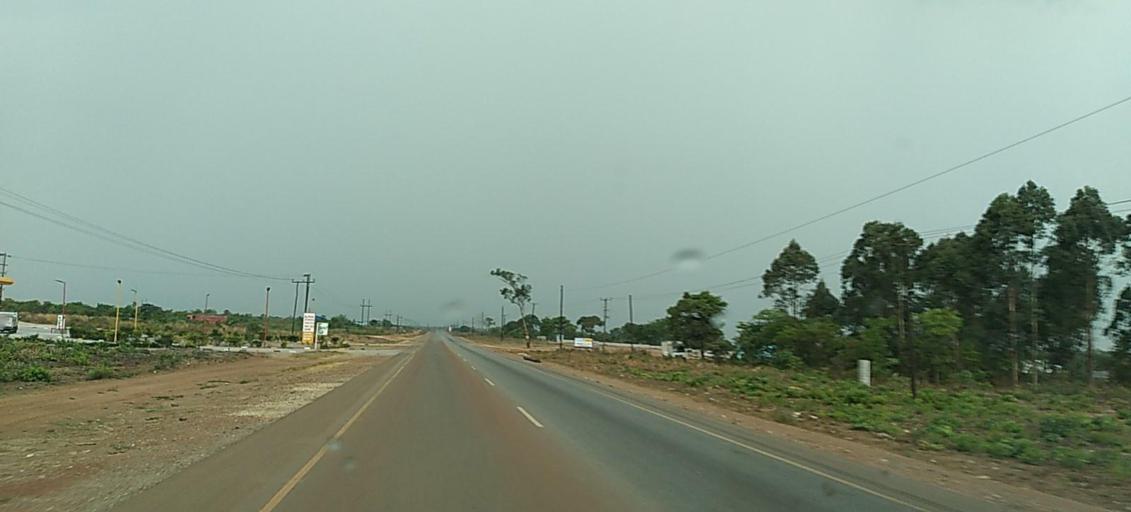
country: ZM
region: Copperbelt
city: Kalulushi
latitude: -12.8346
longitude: 28.1174
